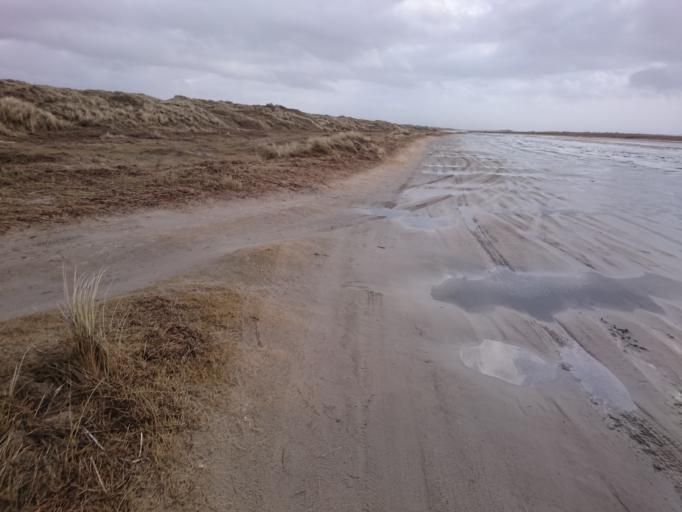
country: DK
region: South Denmark
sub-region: Fano Kommune
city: Nordby
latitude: 55.4256
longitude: 8.3701
